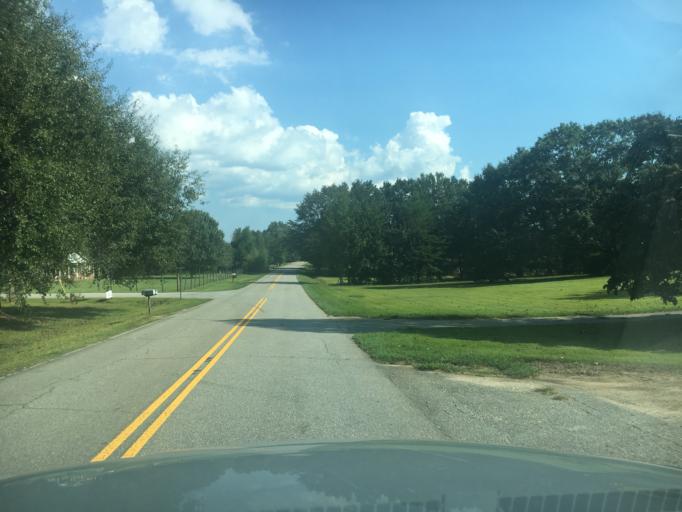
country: US
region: South Carolina
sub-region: Pickens County
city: Liberty
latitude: 34.7429
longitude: -82.6512
